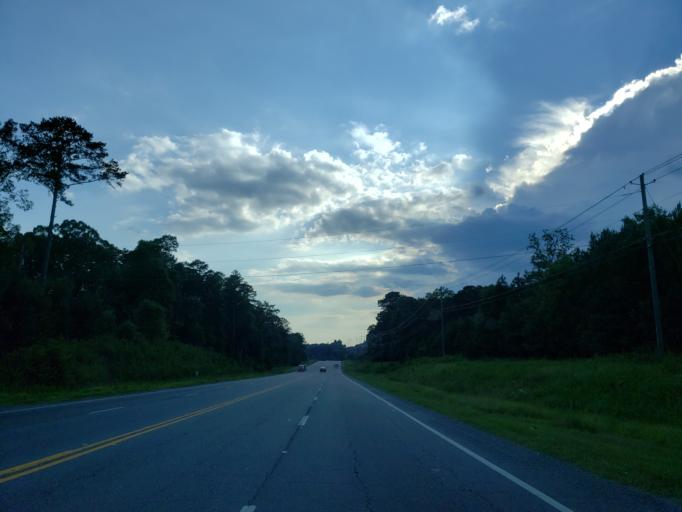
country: US
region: Georgia
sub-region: Bartow County
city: Cartersville
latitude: 34.2190
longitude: -84.7437
